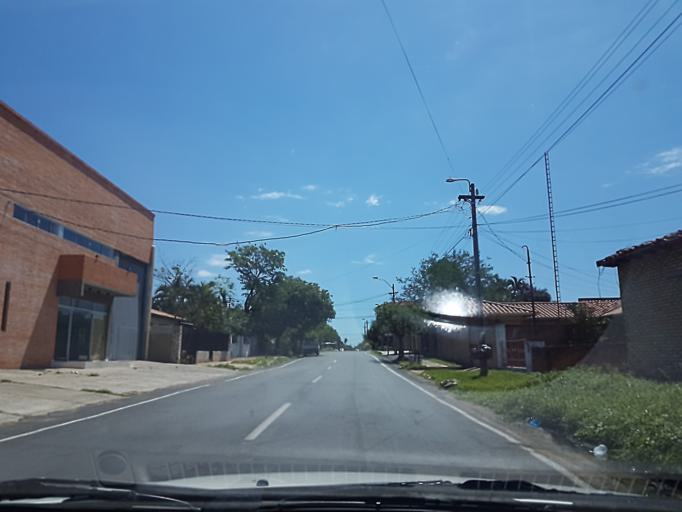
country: PY
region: Central
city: Colonia Mariano Roque Alonso
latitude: -25.2109
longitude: -57.5304
